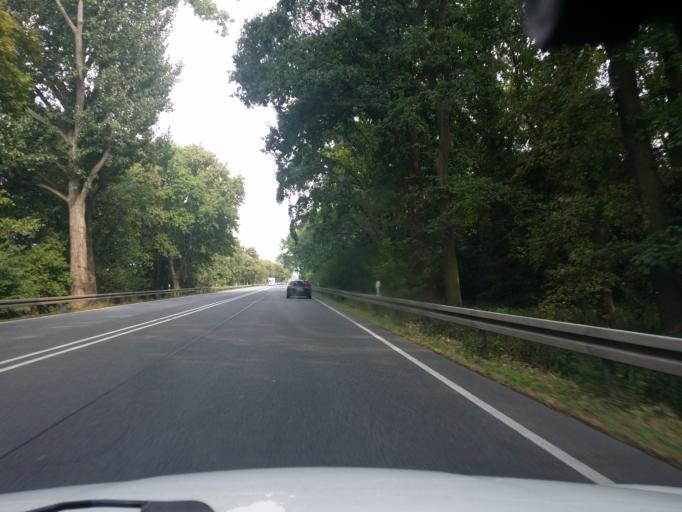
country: DE
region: Hesse
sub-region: Regierungsbezirk Darmstadt
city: Kiedrich
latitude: 50.0176
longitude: 8.0838
